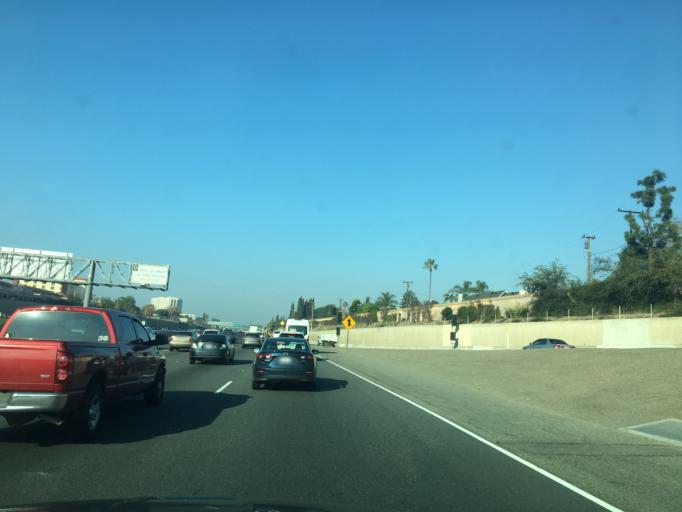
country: US
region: California
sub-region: Orange County
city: Tustin
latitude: 33.7492
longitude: -117.8318
